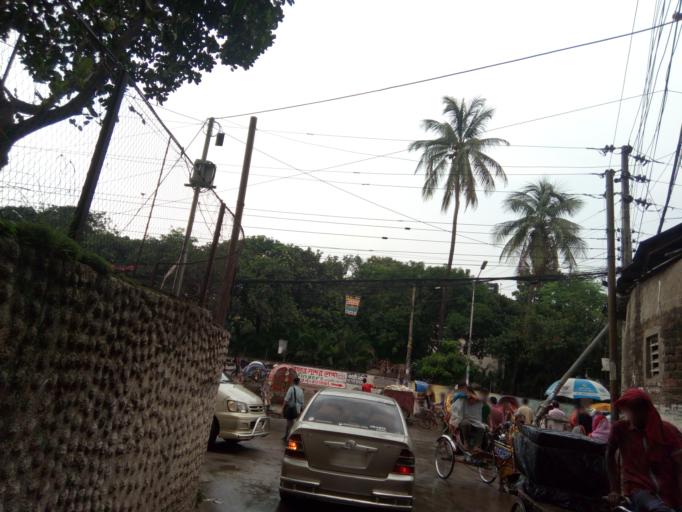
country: BD
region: Dhaka
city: Azimpur
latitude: 23.7579
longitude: 90.3845
